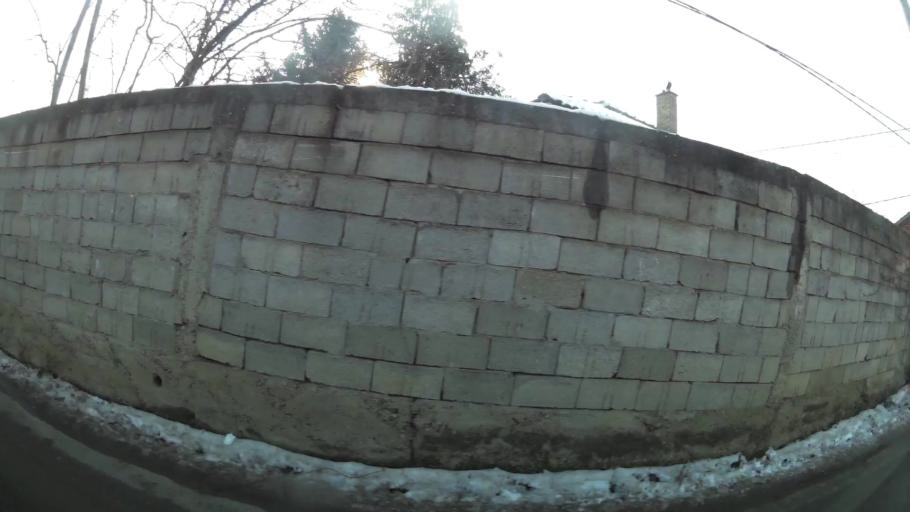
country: MK
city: Creshevo
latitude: 42.0206
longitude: 21.5029
